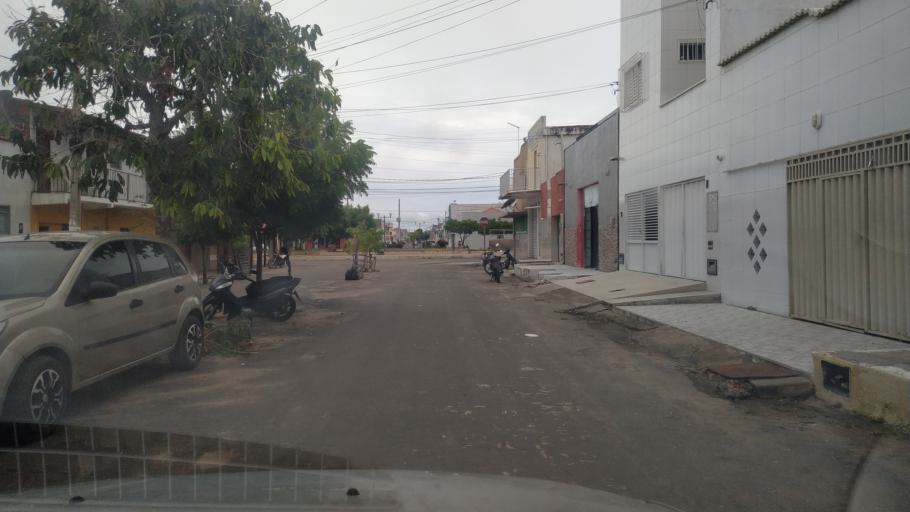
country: BR
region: Rio Grande do Norte
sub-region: Areia Branca
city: Areia Branca
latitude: -4.9582
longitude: -37.1328
